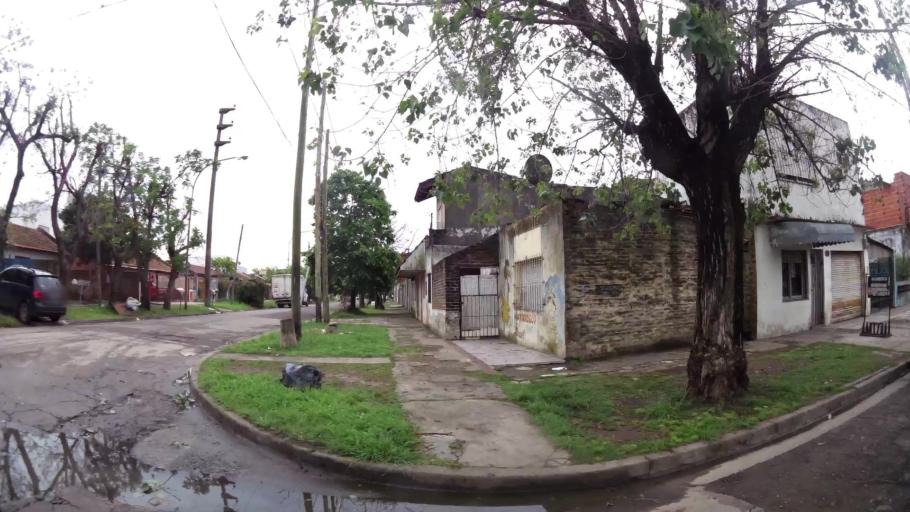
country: AR
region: Buenos Aires
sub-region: Partido de Lanus
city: Lanus
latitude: -34.7316
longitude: -58.3702
